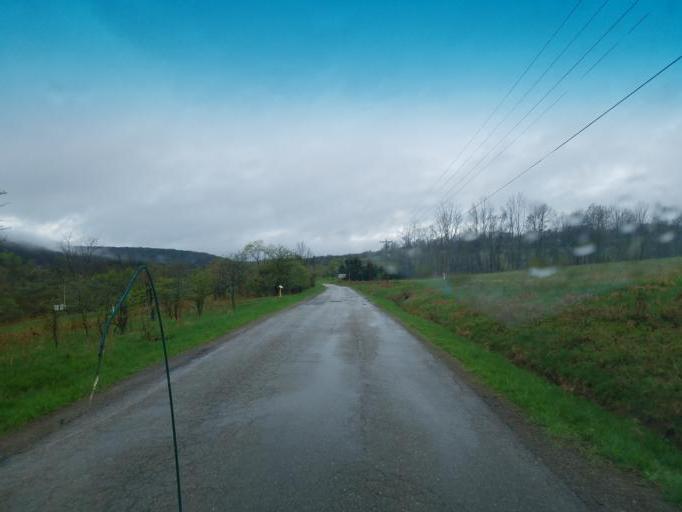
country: US
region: Pennsylvania
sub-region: Tioga County
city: Westfield
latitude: 41.9768
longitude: -77.6755
